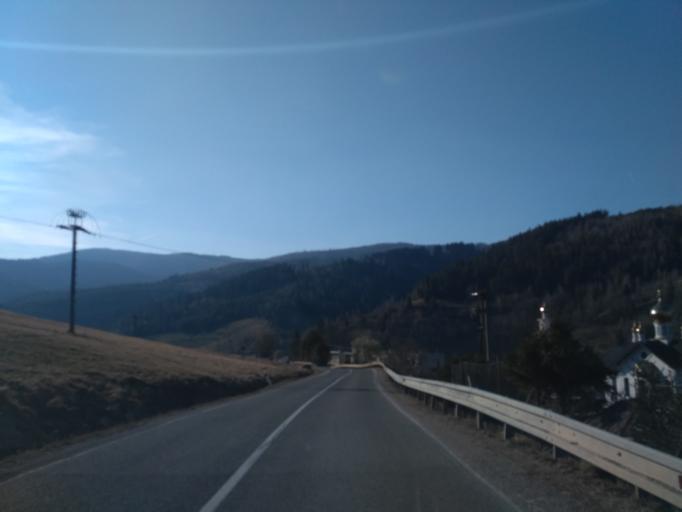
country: SK
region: Kosicky
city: Medzev
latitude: 48.7265
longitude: 20.7320
